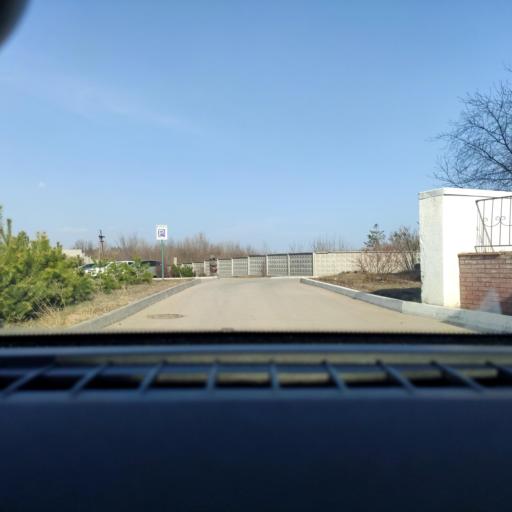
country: RU
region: Samara
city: Tol'yatti
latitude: 53.4987
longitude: 49.3594
